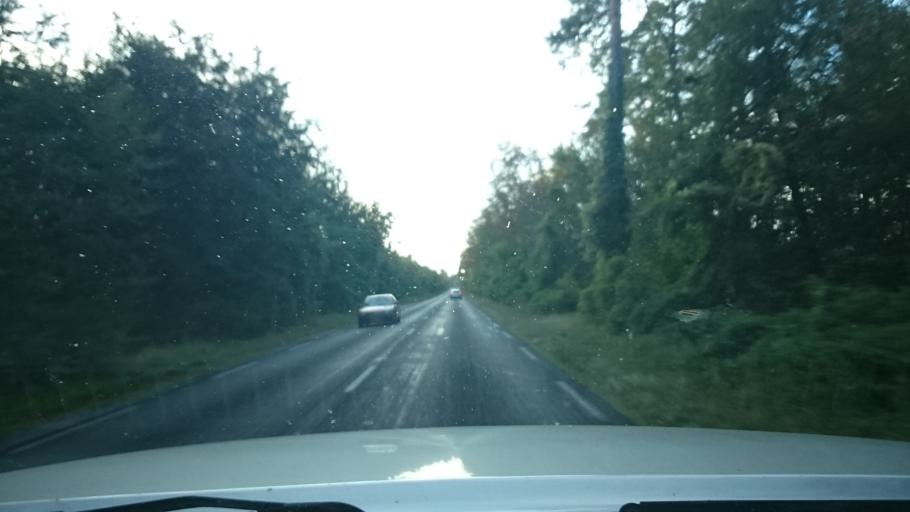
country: FR
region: Ile-de-France
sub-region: Departement de Seine-et-Marne
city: Samois-sur-Seine
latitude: 48.4396
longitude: 2.7275
